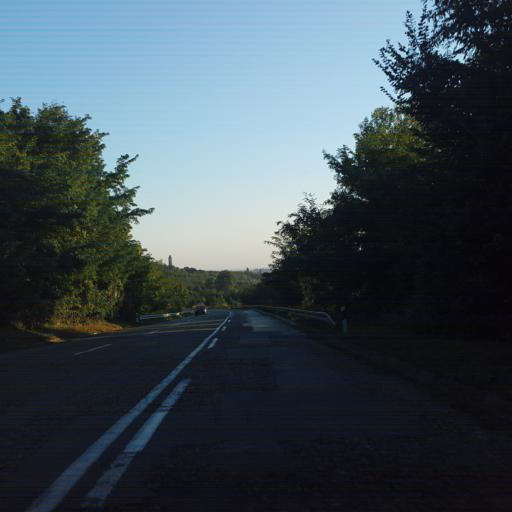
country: RS
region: Central Serbia
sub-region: Borski Okrug
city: Negotin
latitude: 44.2252
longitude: 22.4993
